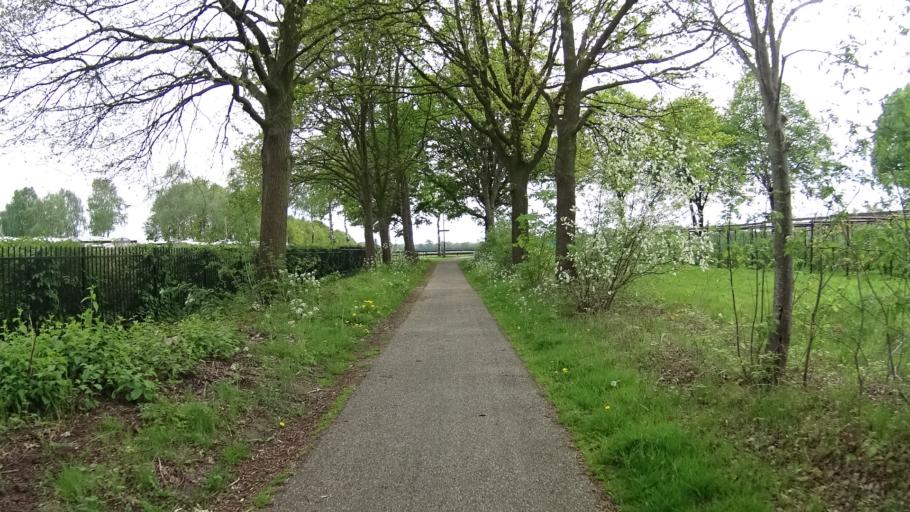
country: NL
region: North Brabant
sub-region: Gemeente Veghel
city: Mariaheide
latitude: 51.6225
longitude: 5.5944
